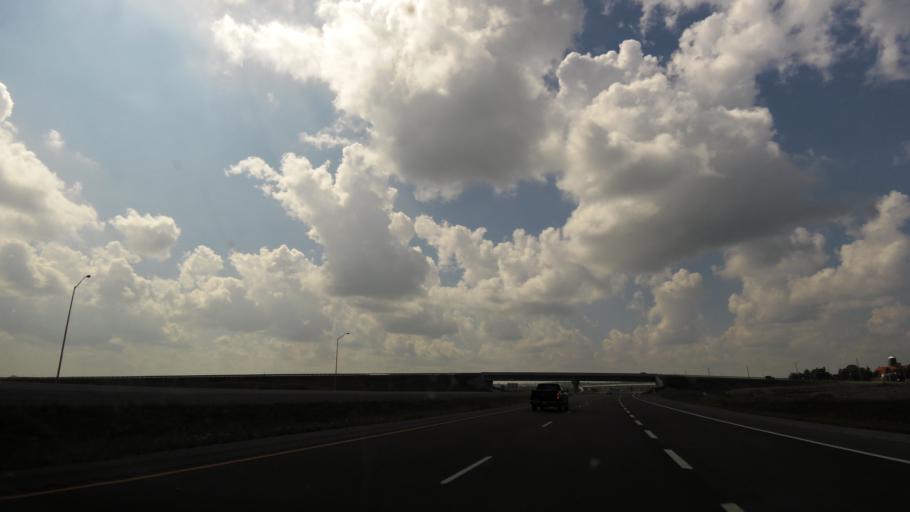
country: CA
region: Ontario
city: Ajax
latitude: 43.9484
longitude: -78.9685
